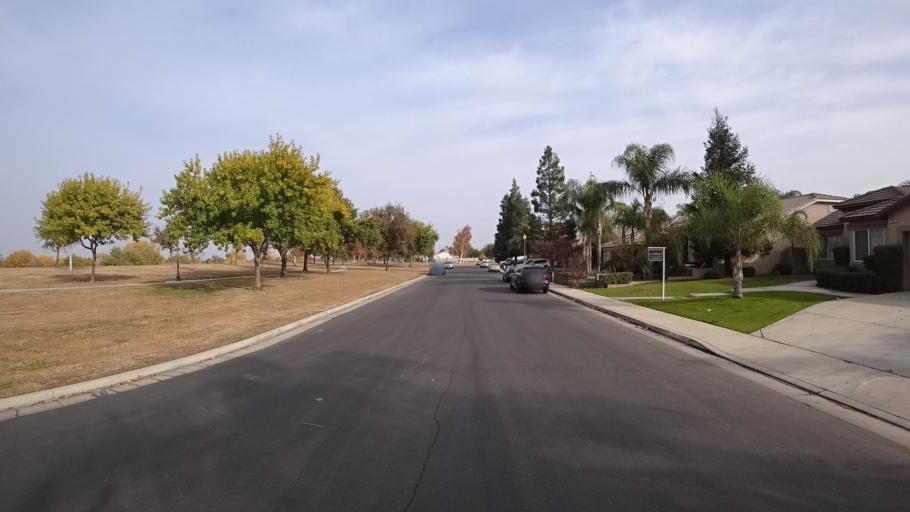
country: US
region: California
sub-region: Kern County
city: Rosedale
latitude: 35.3442
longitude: -119.1446
